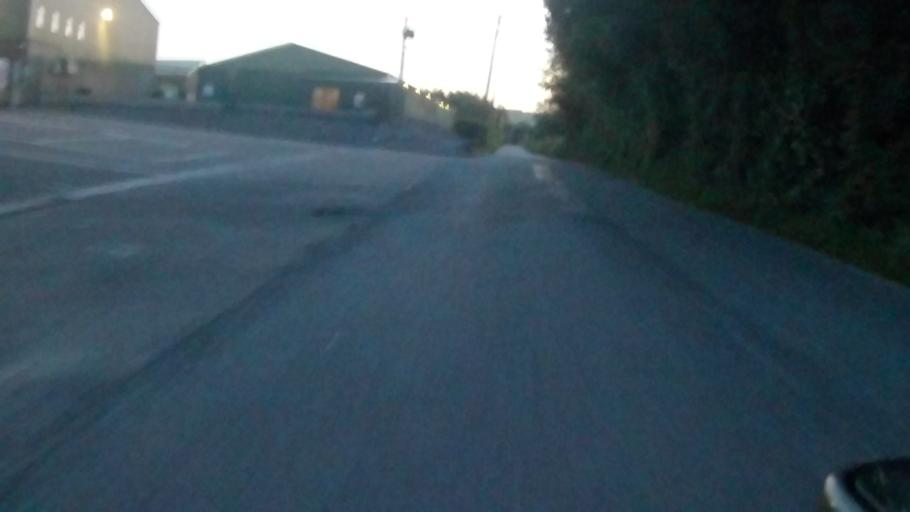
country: IE
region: Munster
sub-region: County Cork
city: Passage West
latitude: 51.9307
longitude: -8.3689
